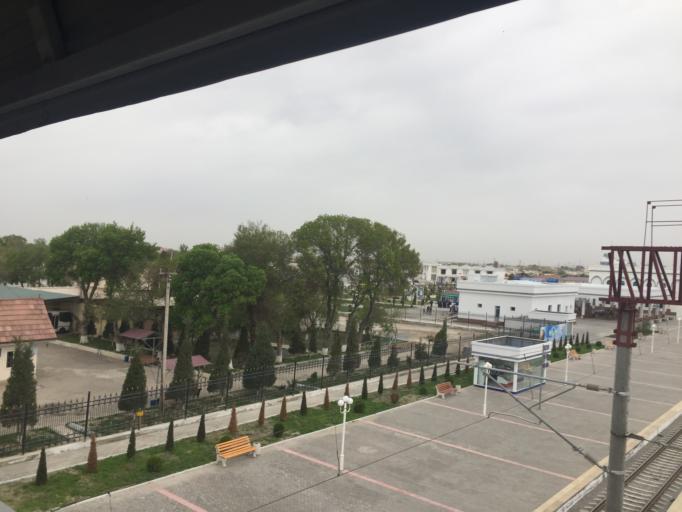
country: UZ
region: Bukhara
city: Kogon
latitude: 39.7211
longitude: 64.5471
